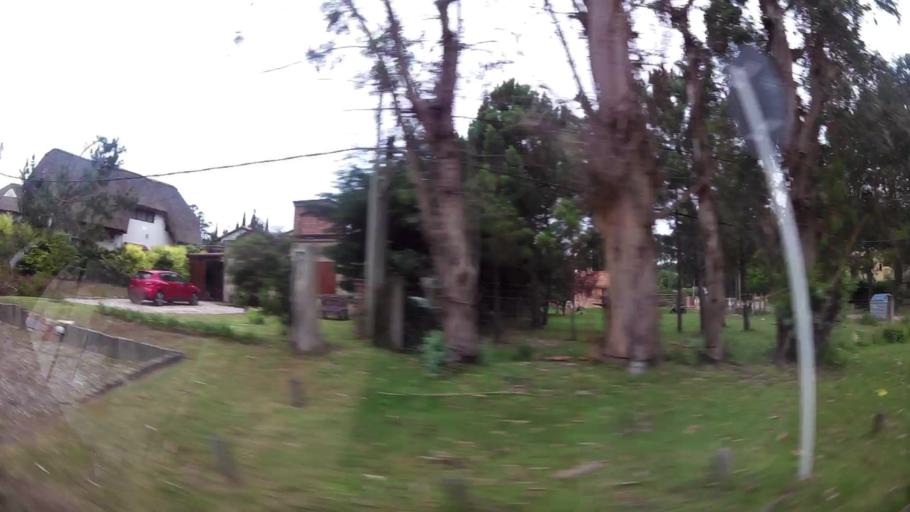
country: UY
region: Maldonado
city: Maldonado
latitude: -34.9008
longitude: -54.9965
